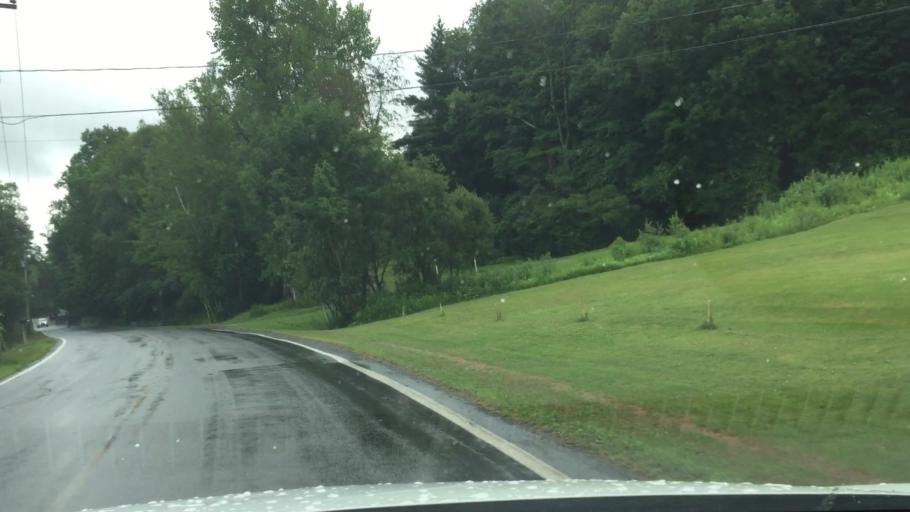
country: US
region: Massachusetts
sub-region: Berkshire County
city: Pittsfield
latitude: 42.4194
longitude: -73.2858
